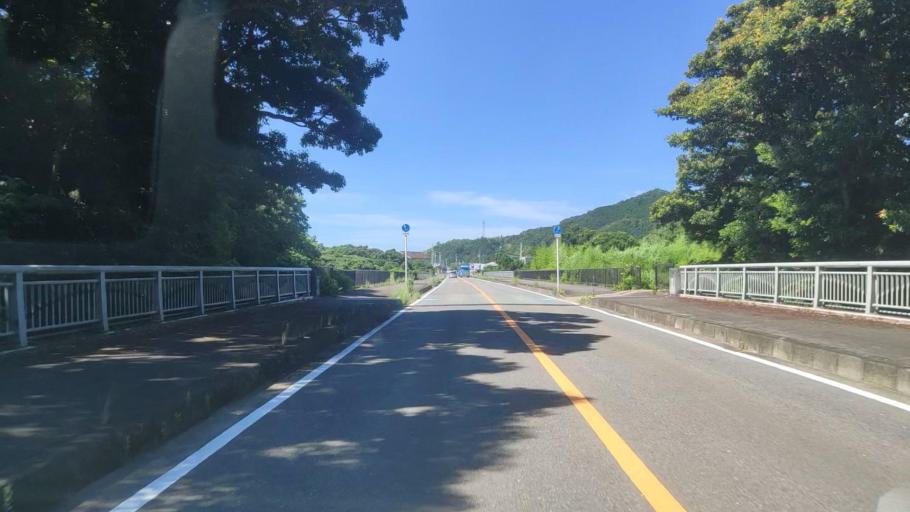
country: JP
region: Wakayama
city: Shingu
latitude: 33.7082
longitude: 135.9953
